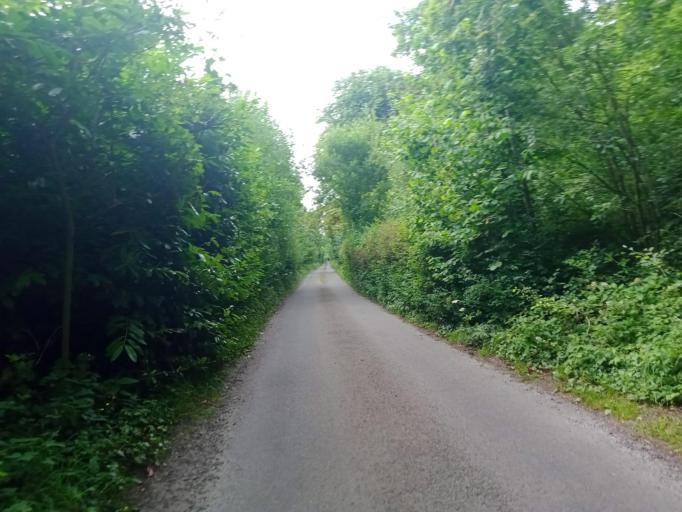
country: IE
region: Leinster
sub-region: Laois
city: Abbeyleix
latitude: 52.9057
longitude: -7.3615
